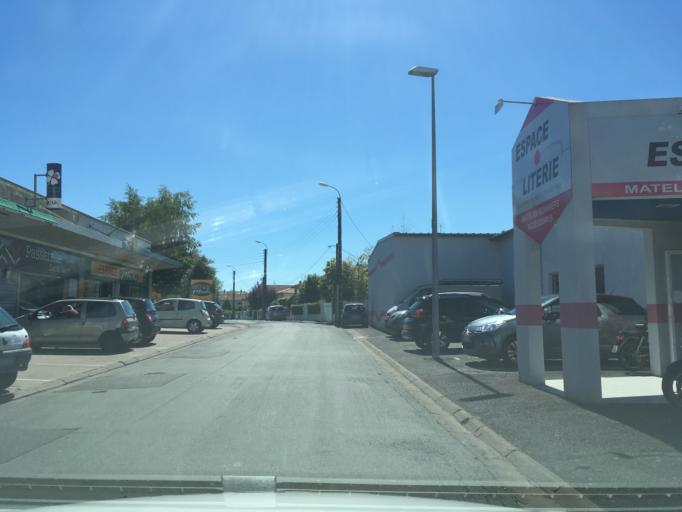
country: FR
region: Poitou-Charentes
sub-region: Departement des Deux-Sevres
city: Niort
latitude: 46.3273
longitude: -0.4376
